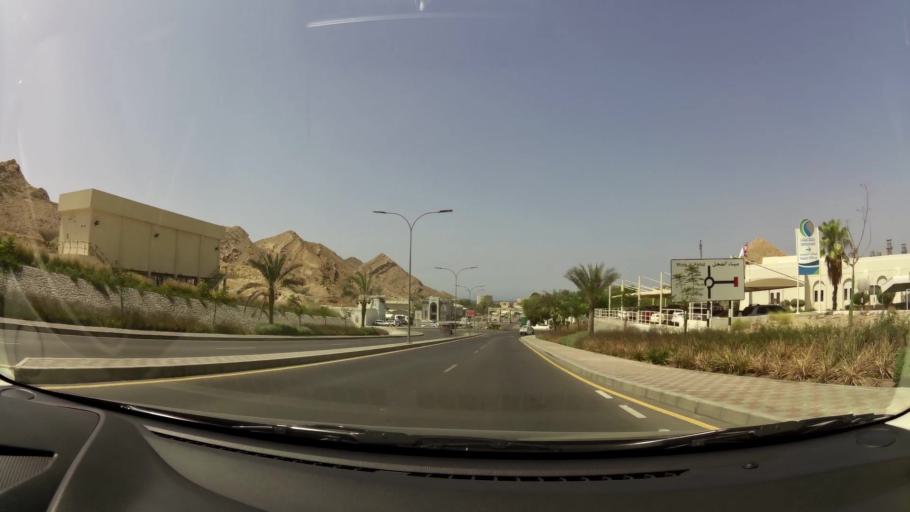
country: OM
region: Muhafazat Masqat
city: Muscat
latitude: 23.6240
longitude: 58.5077
